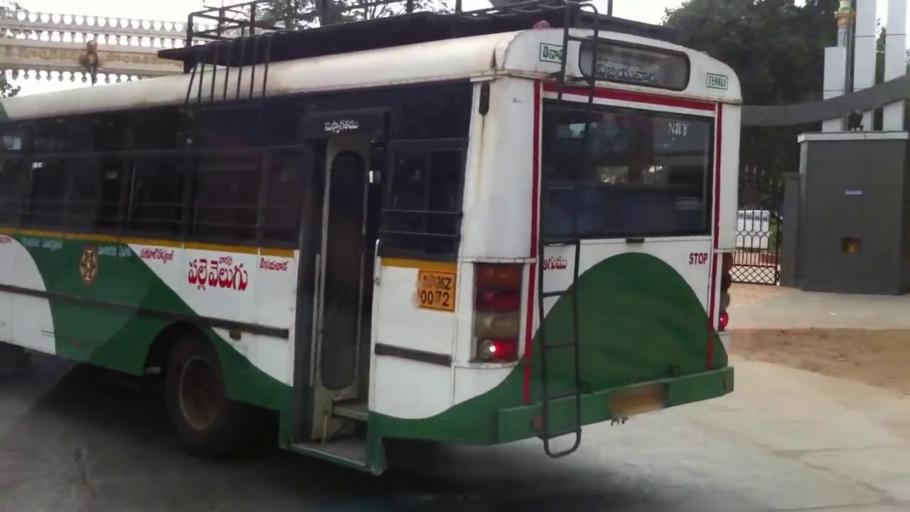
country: IN
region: Andhra Pradesh
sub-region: Guntur
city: Bhattiprolu
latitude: 16.2282
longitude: 80.6518
